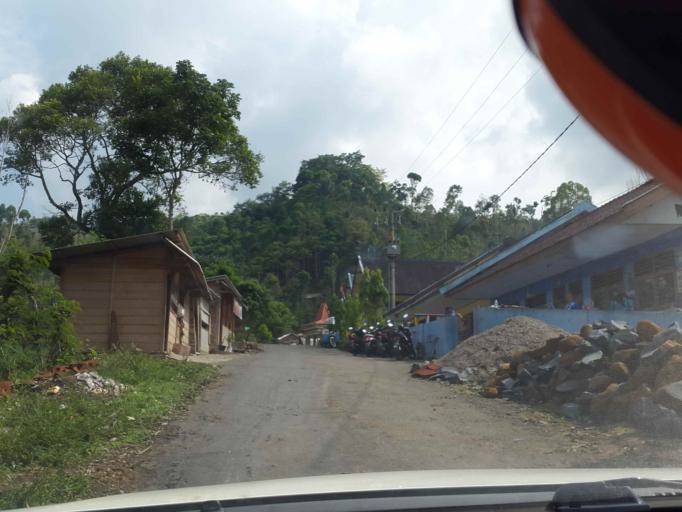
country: ID
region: East Java
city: Ponorogo
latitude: -7.7991
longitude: 111.6460
